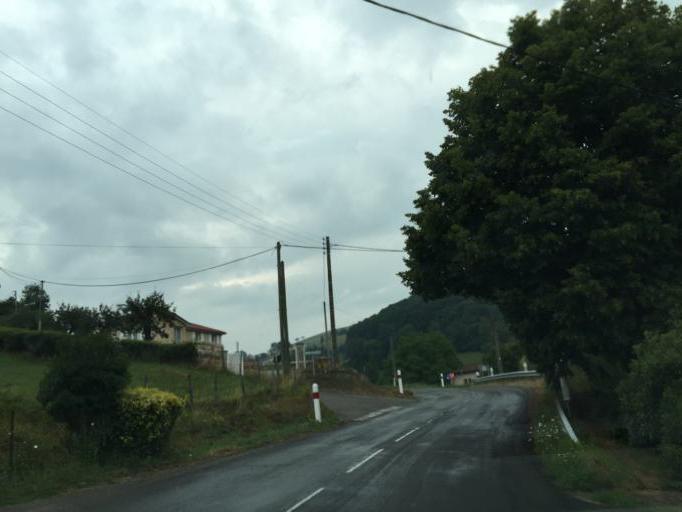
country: FR
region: Rhone-Alpes
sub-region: Departement de la Loire
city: Sorbiers
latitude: 45.5175
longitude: 4.4450
